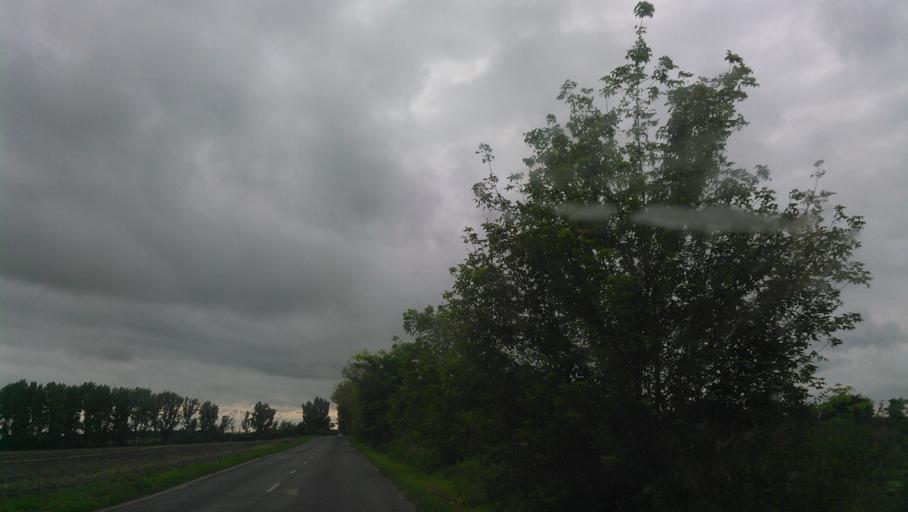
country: SK
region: Trnavsky
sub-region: Okres Dunajska Streda
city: Velky Meder
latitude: 47.9211
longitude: 17.7421
